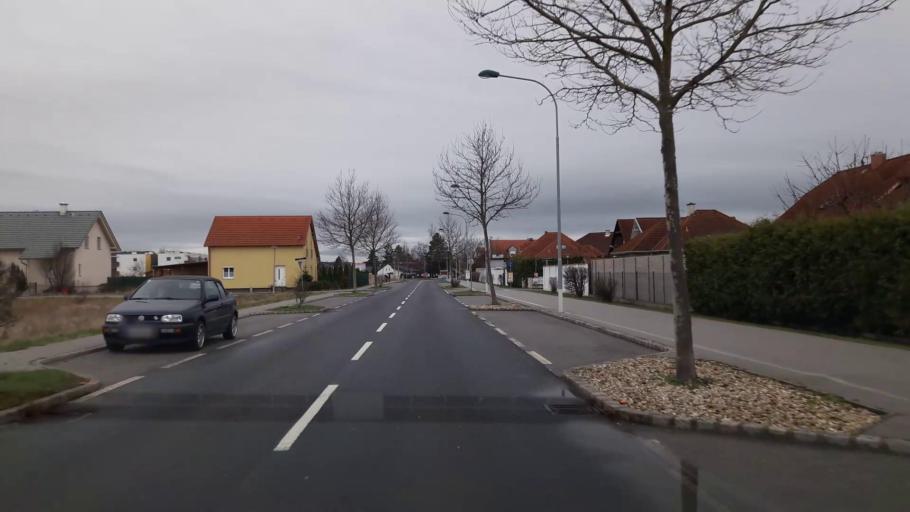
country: AT
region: Burgenland
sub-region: Politischer Bezirk Neusiedl am See
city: Bruckneudorf
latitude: 48.0378
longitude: 16.7841
